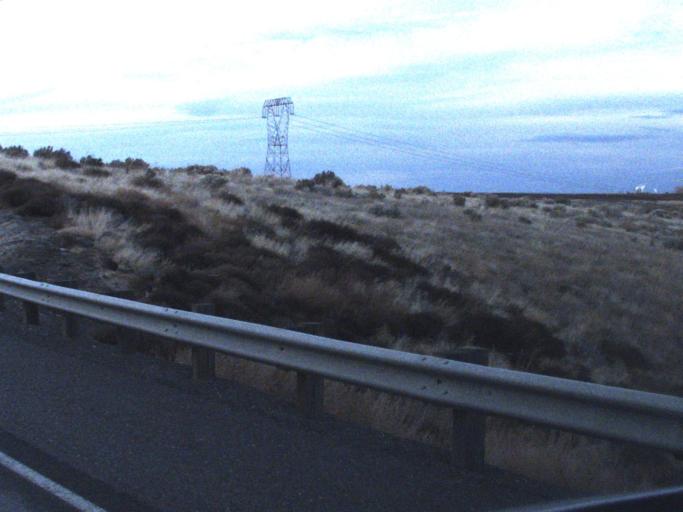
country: US
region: Washington
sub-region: Benton County
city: Finley
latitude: 46.0536
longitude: -118.8854
